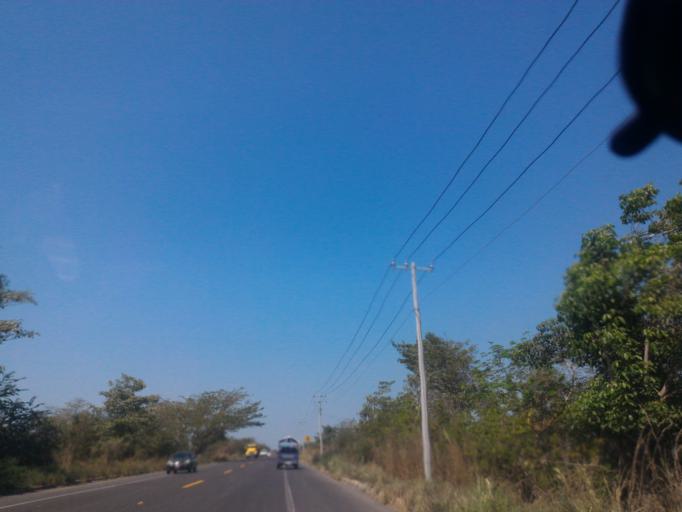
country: MX
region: Michoacan
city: Coahuayana Viejo
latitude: 18.7677
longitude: -103.7366
